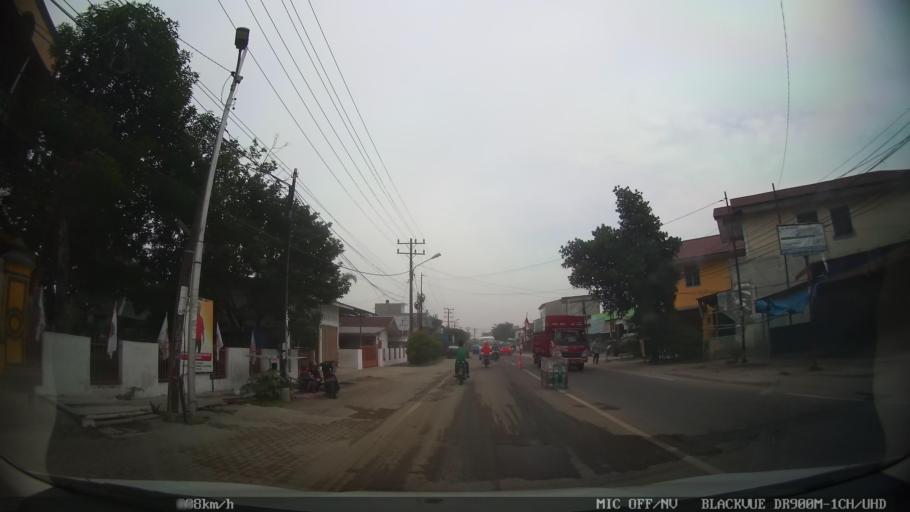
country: ID
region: North Sumatra
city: Deli Tua
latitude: 3.5471
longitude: 98.7167
